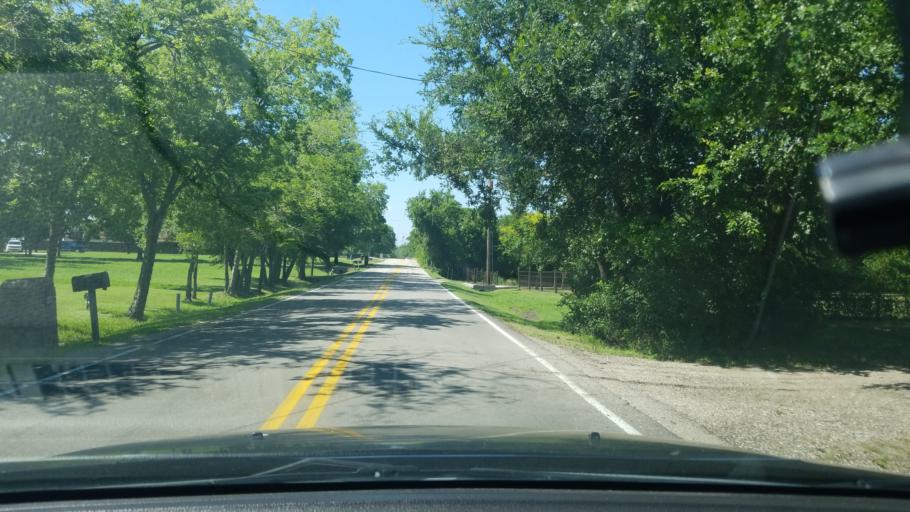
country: US
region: Texas
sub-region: Dallas County
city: Sunnyvale
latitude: 32.7871
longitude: -96.5550
